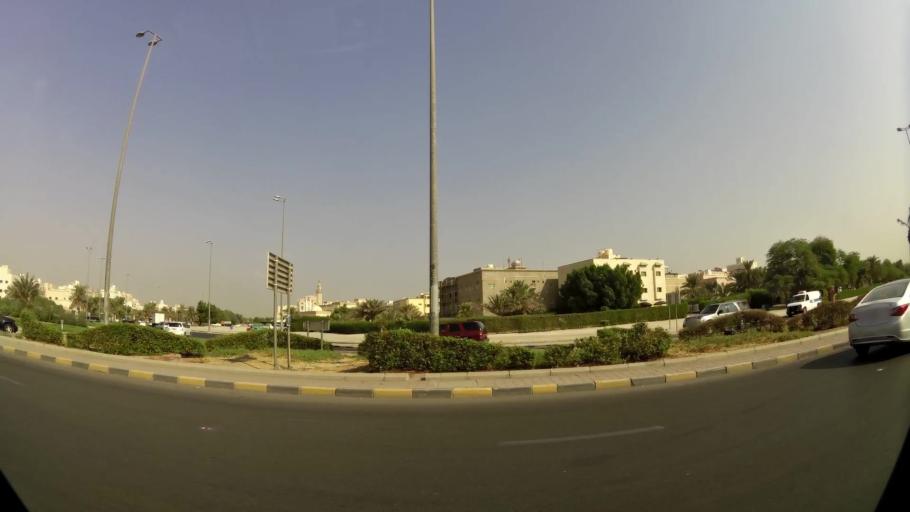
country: KW
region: Al Asimah
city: Ar Rabiyah
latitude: 29.2751
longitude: 47.8896
